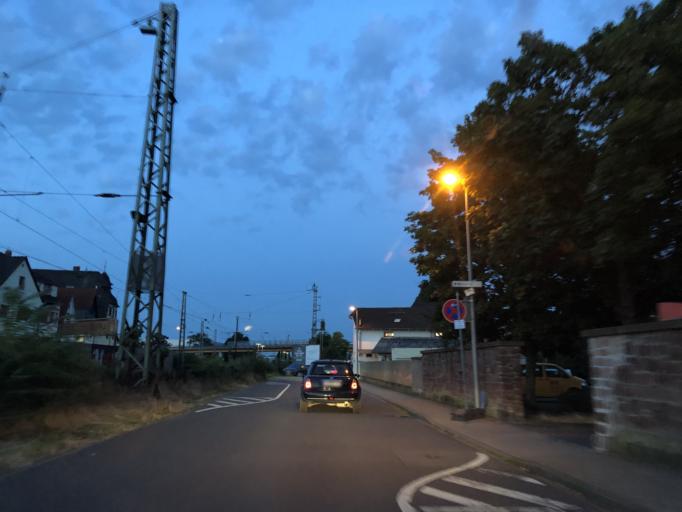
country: DE
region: Hesse
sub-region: Regierungsbezirk Darmstadt
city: Gross-Gerau
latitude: 49.9254
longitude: 8.4819
